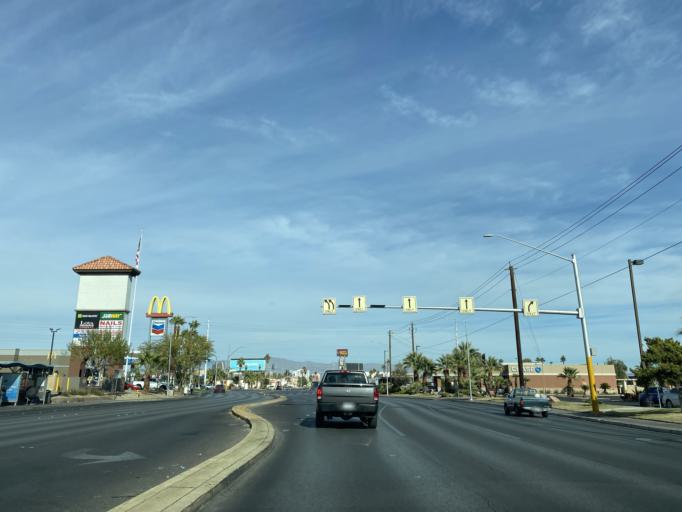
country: US
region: Nevada
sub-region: Clark County
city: Winchester
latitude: 36.1427
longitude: -115.1369
